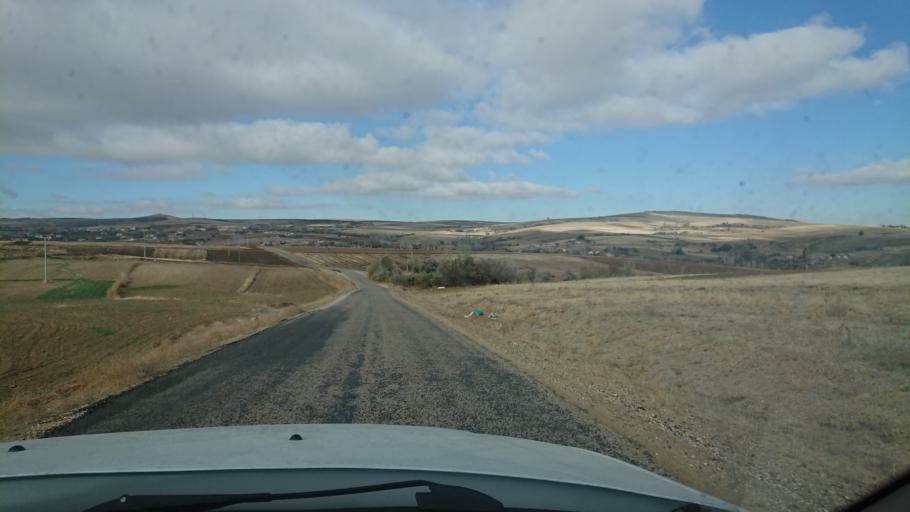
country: TR
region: Aksaray
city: Agacoren
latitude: 38.8182
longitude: 33.9793
